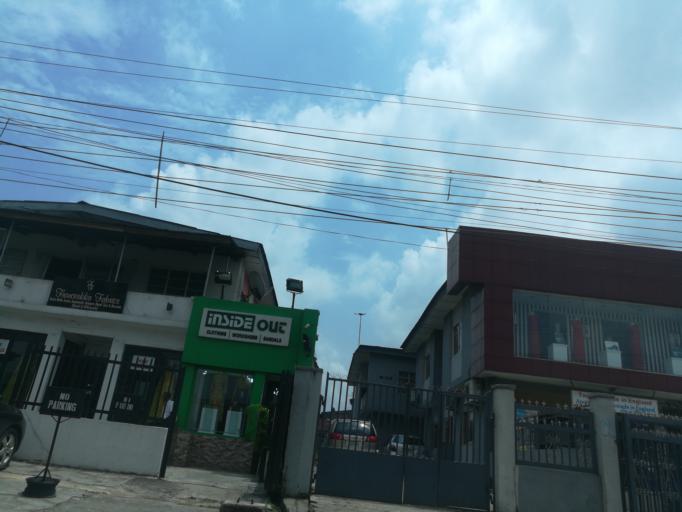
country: NG
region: Lagos
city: Ikeja
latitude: 6.5900
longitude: 3.3609
